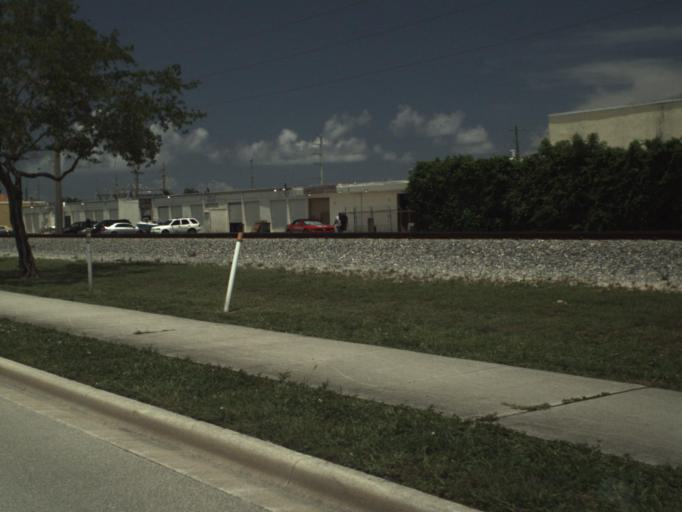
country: US
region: Florida
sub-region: Broward County
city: Deerfield Beach
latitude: 26.3019
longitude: -80.1061
